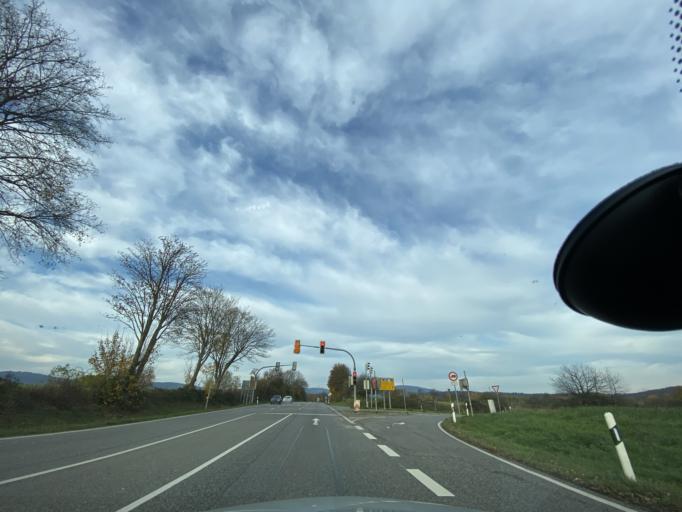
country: DE
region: Hesse
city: Kelkheim (Taunus)
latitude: 50.1561
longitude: 8.4610
